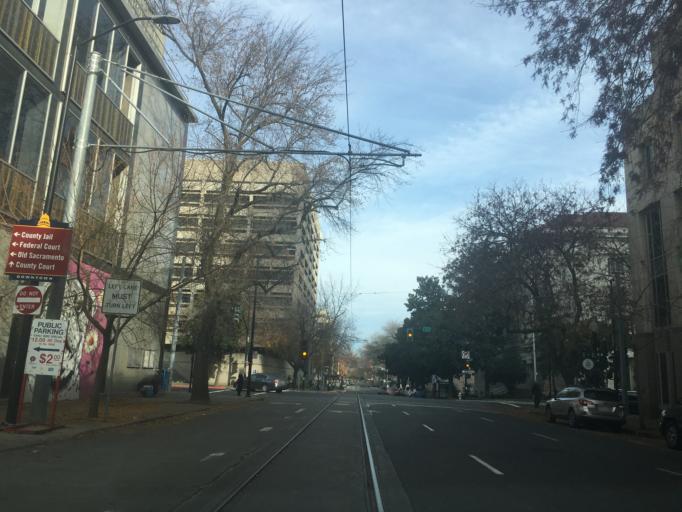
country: US
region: California
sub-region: Sacramento County
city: Sacramento
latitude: 38.5817
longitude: -121.4959
